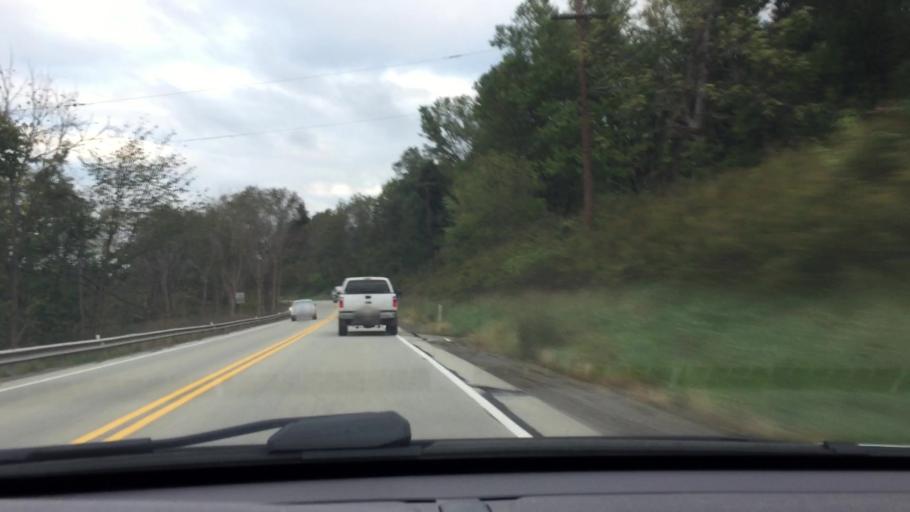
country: US
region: Pennsylvania
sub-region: Washington County
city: Canonsburg
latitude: 40.2227
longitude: -80.1567
